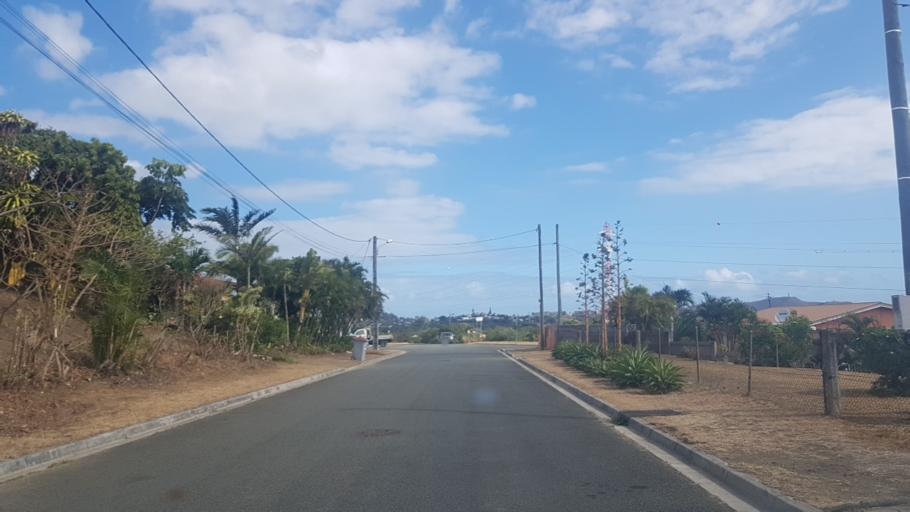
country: NC
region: South Province
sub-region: Dumbea
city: Dumbea
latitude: -22.2091
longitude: 166.4580
